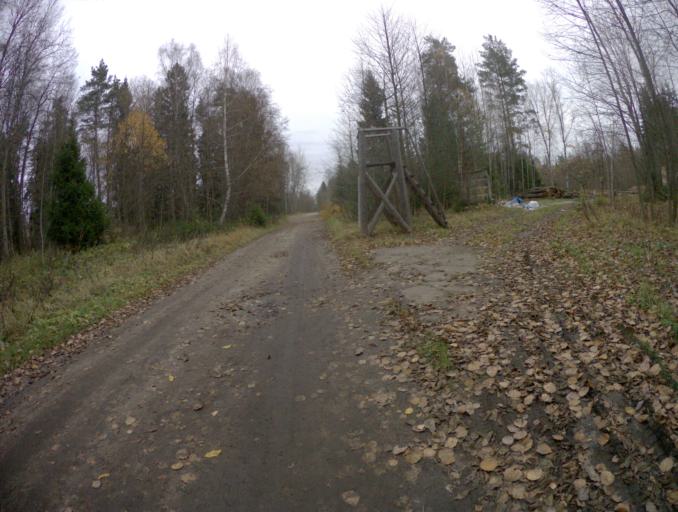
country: RU
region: Vladimir
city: Krasnyy Oktyabr'
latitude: 56.0146
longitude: 38.8512
